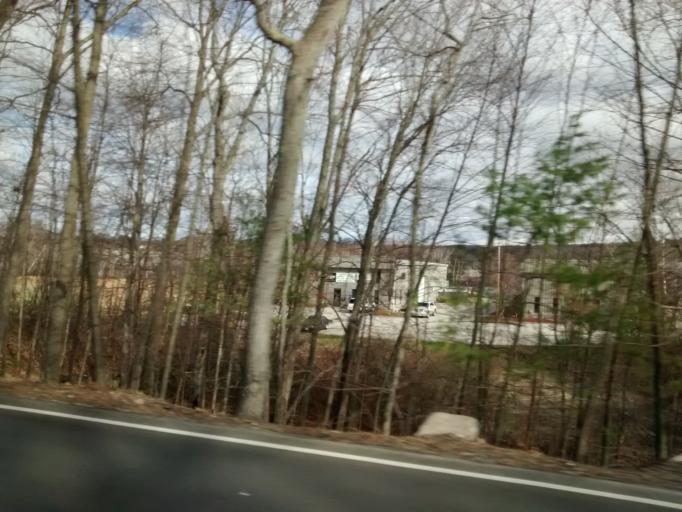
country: US
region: Massachusetts
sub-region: Worcester County
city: Whitinsville
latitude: 42.1084
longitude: -71.6773
